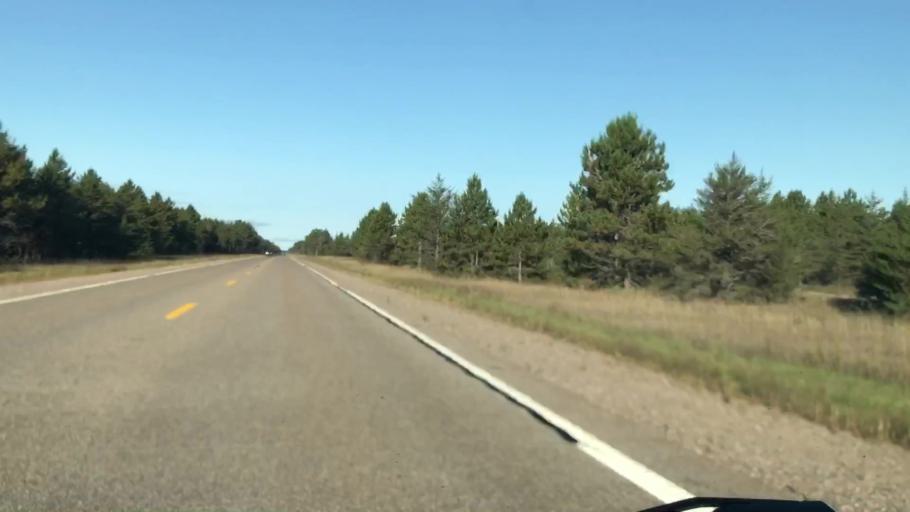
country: US
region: Michigan
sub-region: Chippewa County
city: Sault Ste. Marie
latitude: 46.3587
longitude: -84.8250
